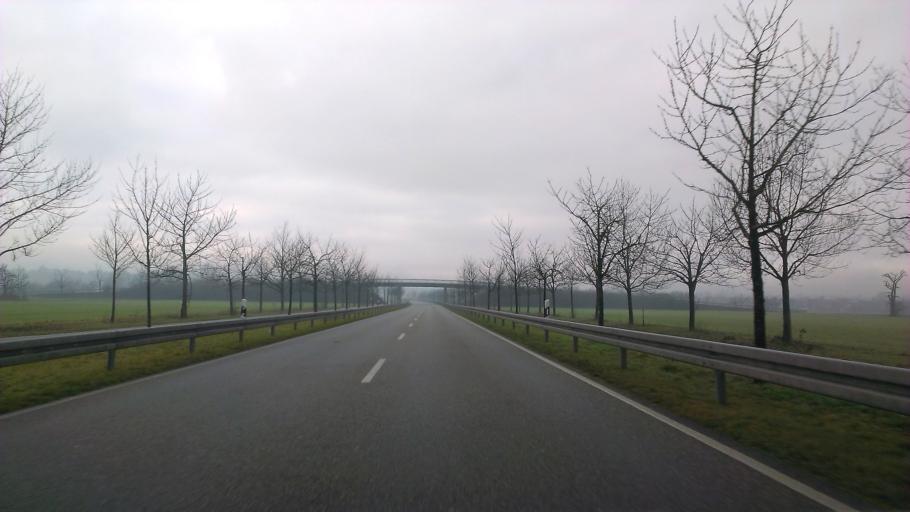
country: DE
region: Baden-Wuerttemberg
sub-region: Karlsruhe Region
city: Waghausel
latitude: 49.2329
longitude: 8.5516
